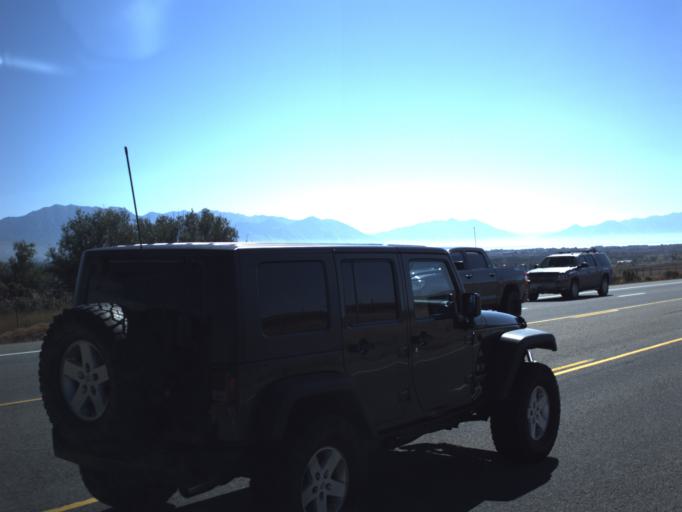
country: US
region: Utah
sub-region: Salt Lake County
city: Bluffdale
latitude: 40.4234
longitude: -111.9262
